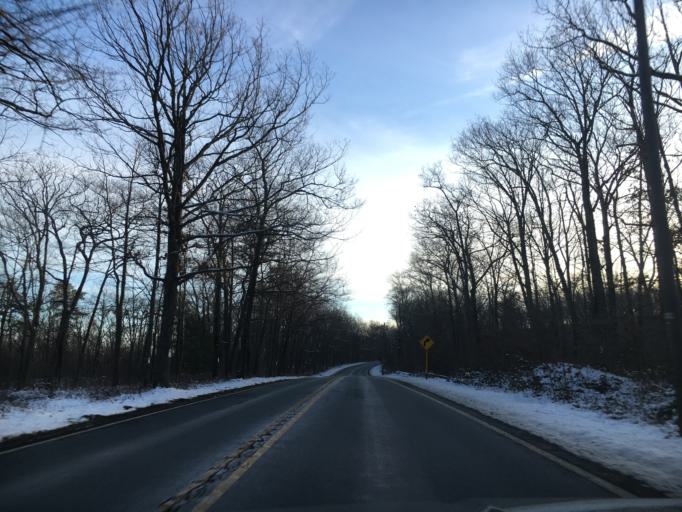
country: US
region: Pennsylvania
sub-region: Pike County
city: Hemlock Farms
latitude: 41.3564
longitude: -75.1289
